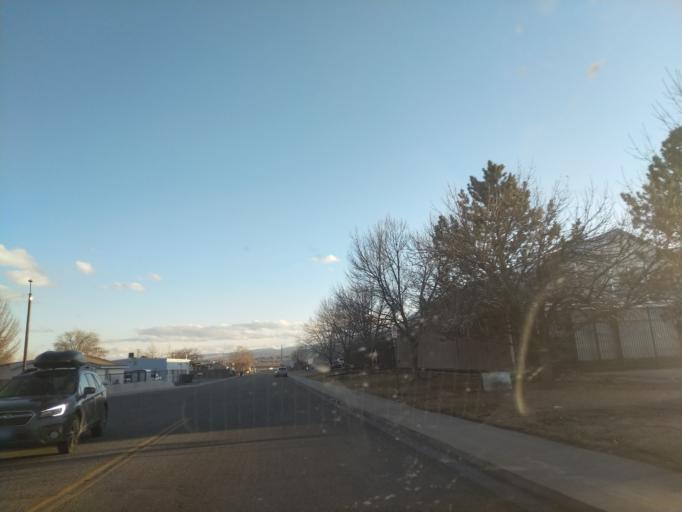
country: US
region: Colorado
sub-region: Mesa County
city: Fruitvale
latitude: 39.0759
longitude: -108.5175
